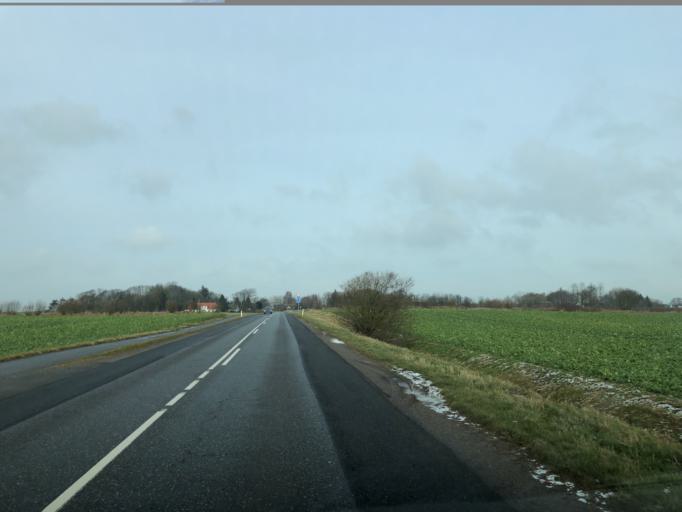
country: DK
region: South Denmark
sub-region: Vejle Kommune
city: Jelling
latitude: 55.7710
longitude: 9.4252
